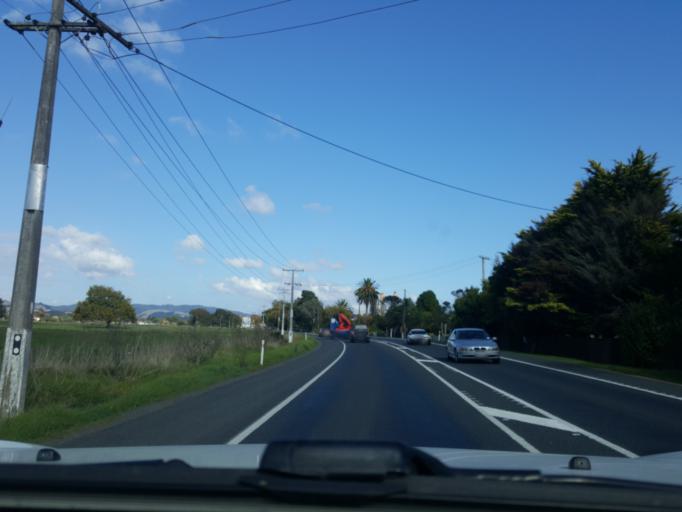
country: NZ
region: Waikato
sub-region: Waikato District
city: Te Kauwhata
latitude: -37.5231
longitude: 175.1609
